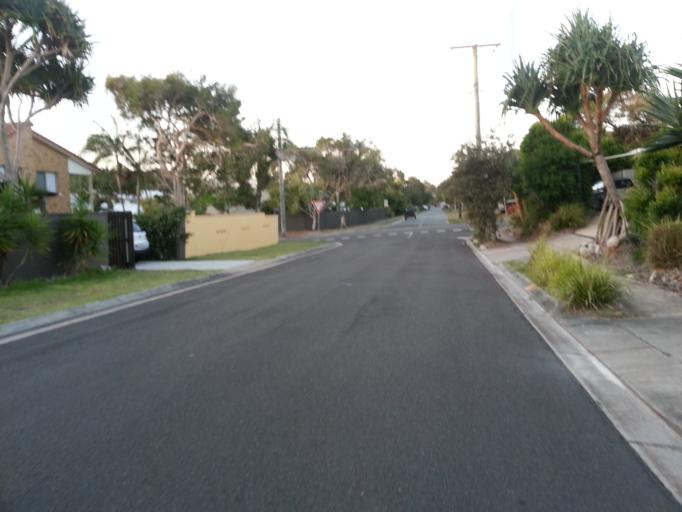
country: AU
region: Queensland
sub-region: Sunshine Coast
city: Peregian Springs
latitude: -26.4917
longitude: 153.0940
